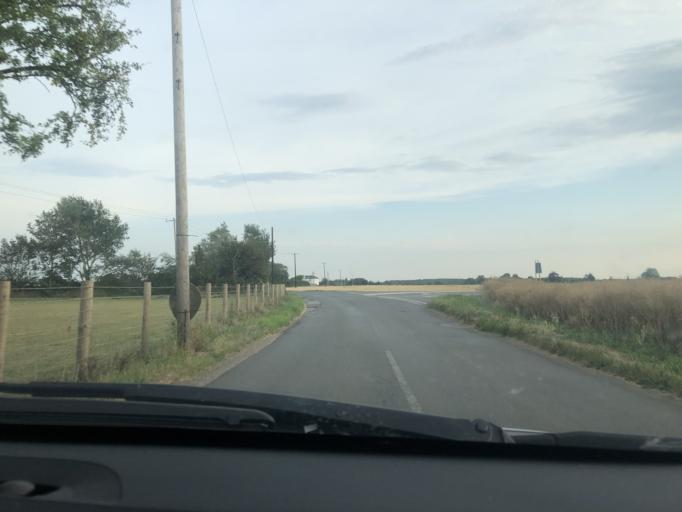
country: GB
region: England
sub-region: Kent
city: Herne Bay
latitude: 51.3561
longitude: 1.1677
